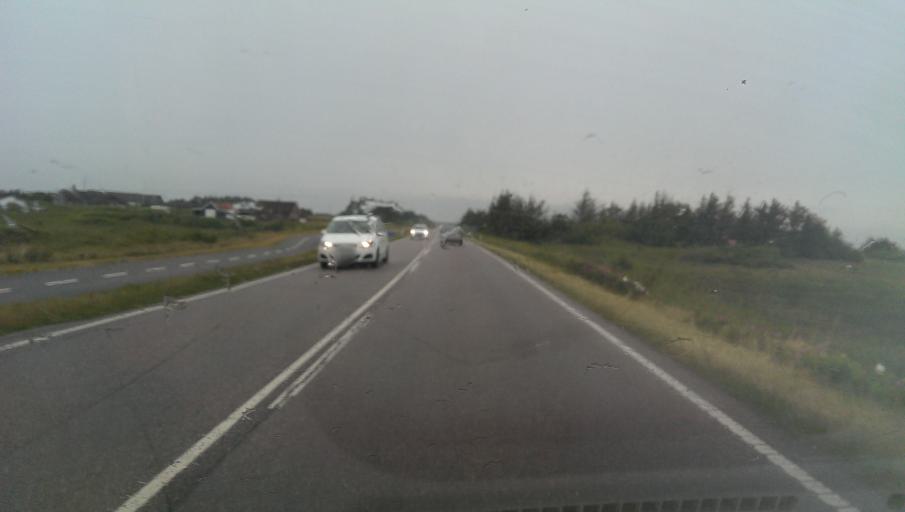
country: DK
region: Central Jutland
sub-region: Ringkobing-Skjern Kommune
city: Hvide Sande
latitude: 56.0638
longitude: 8.1224
